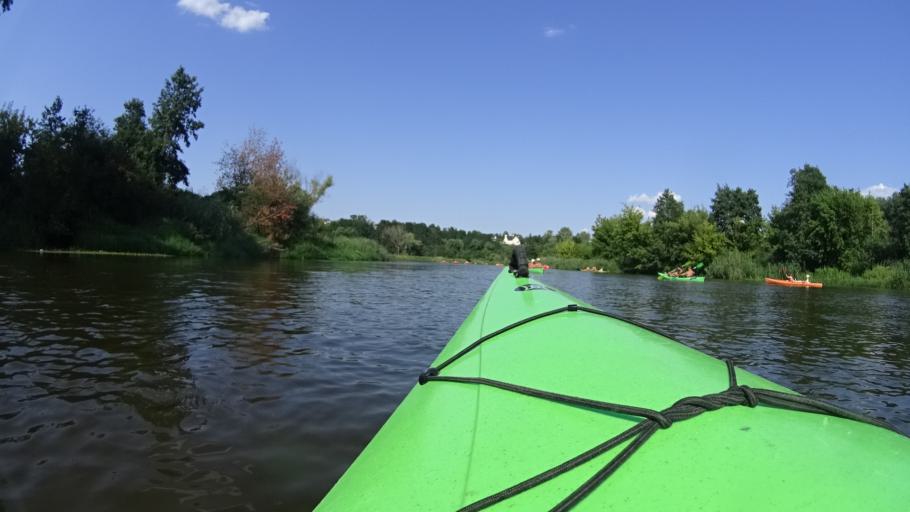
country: PL
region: Masovian Voivodeship
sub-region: Powiat bialobrzeski
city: Bialobrzegi
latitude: 51.6639
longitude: 20.9081
